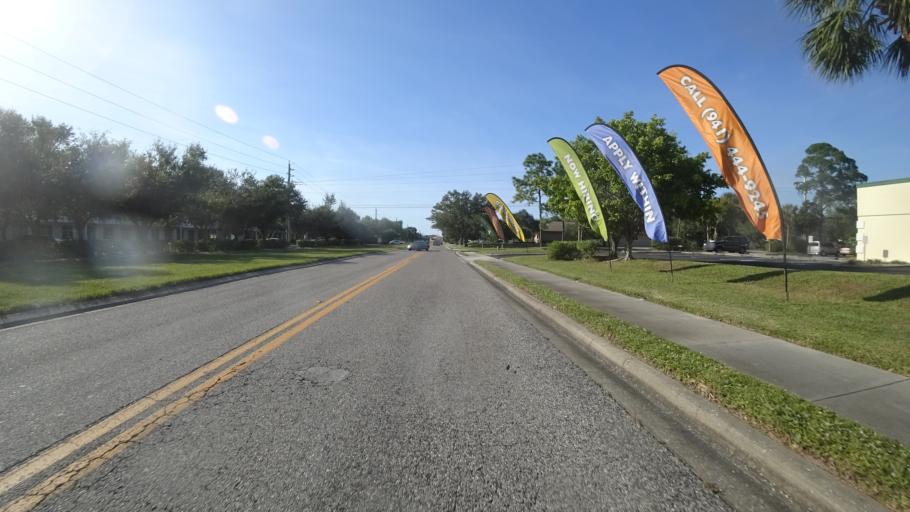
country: US
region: Florida
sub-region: Manatee County
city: Whitfield
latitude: 27.4044
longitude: -82.5528
